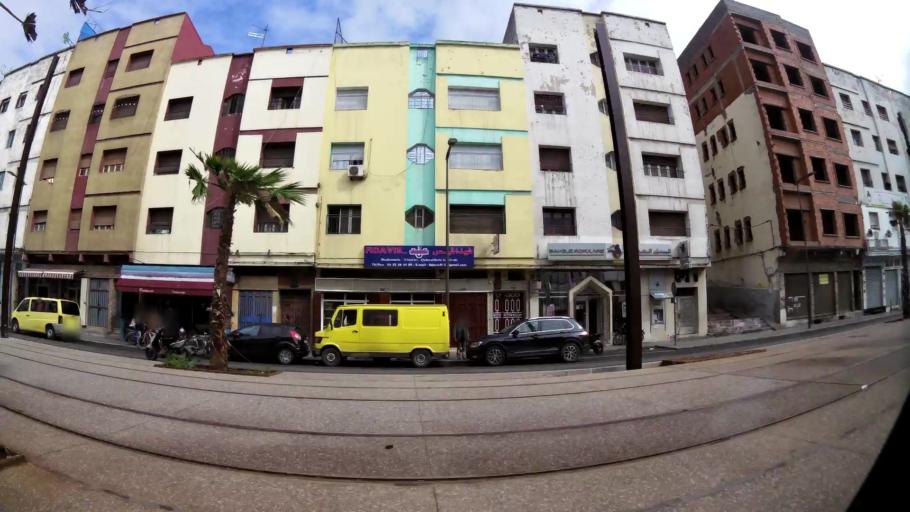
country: MA
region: Grand Casablanca
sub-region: Casablanca
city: Casablanca
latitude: 33.5721
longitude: -7.5828
